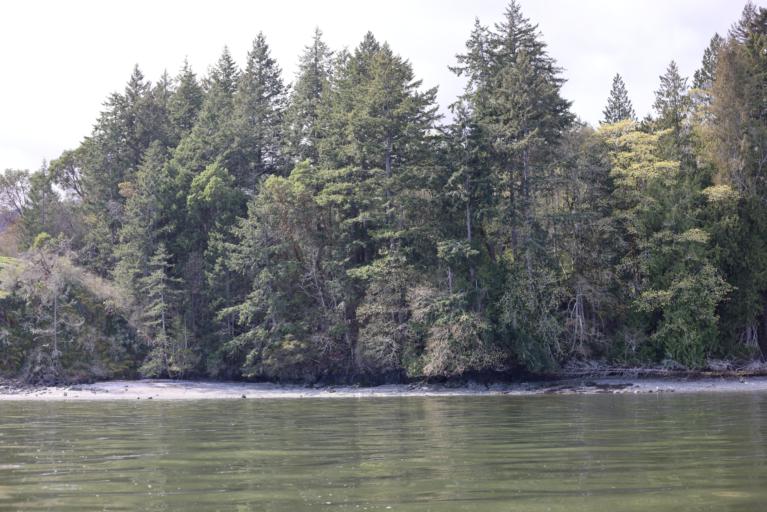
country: CA
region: British Columbia
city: North Saanich
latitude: 48.6180
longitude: -123.5197
